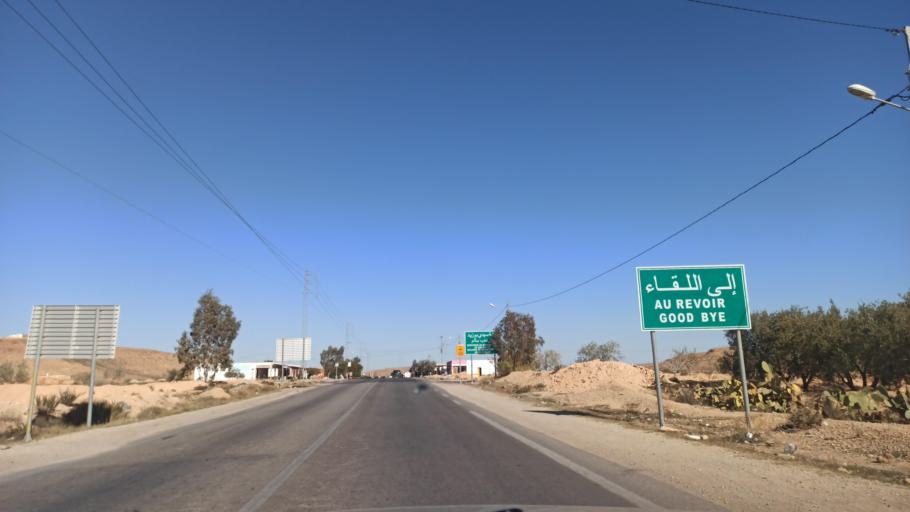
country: TN
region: Sidi Bu Zayd
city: Bi'r al Hufayy
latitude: 34.7026
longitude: 9.0441
